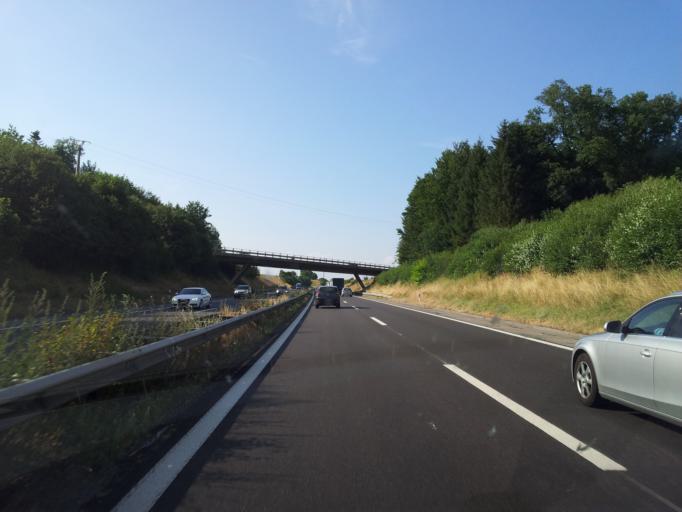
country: CH
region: Fribourg
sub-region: Sarine District
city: Matran
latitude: 46.7362
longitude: 7.0873
